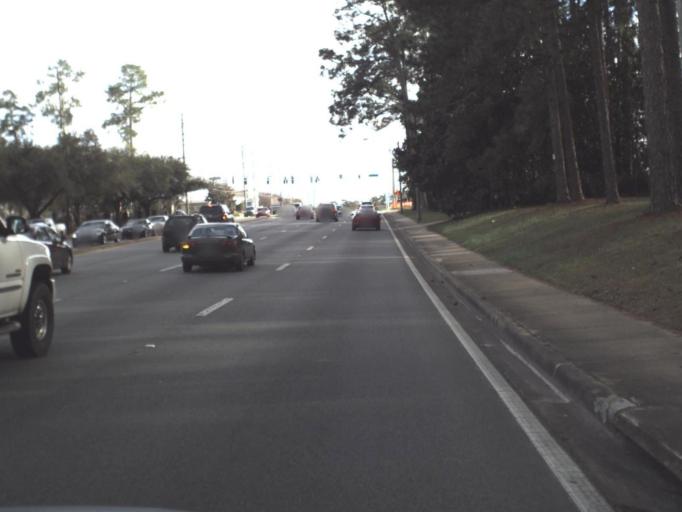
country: US
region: Florida
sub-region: Leon County
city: Tallahassee
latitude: 30.4412
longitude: -84.2619
